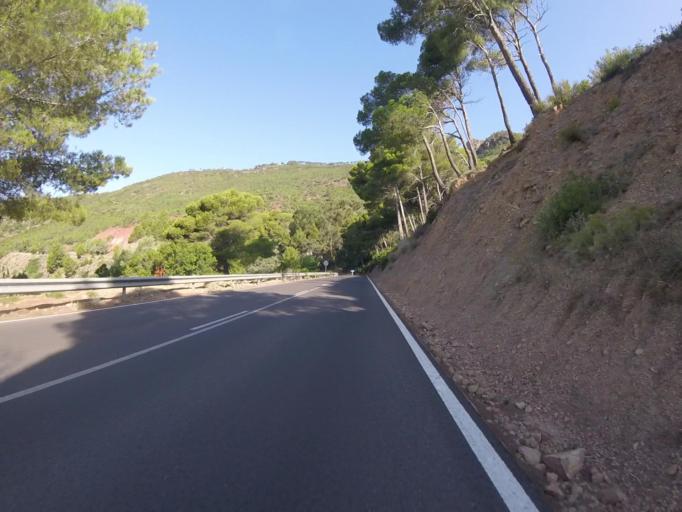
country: ES
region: Valencia
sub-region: Provincia de Castello
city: Benicassim
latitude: 40.0787
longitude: 0.0336
